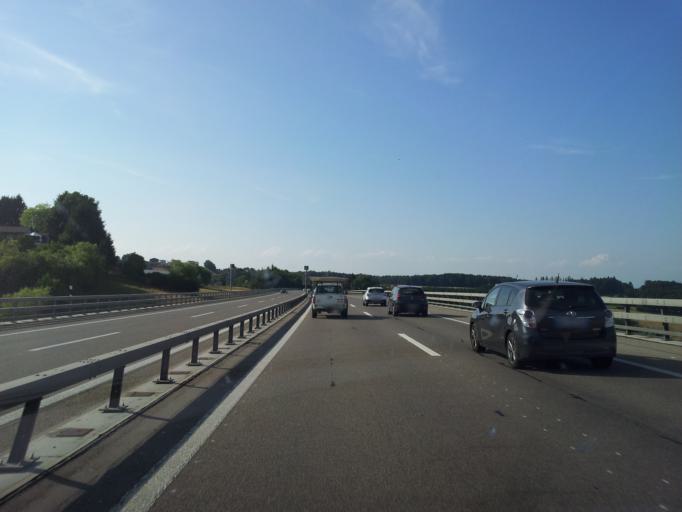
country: CH
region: Fribourg
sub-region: Gruyere District
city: La Roche
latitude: 46.6962
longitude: 7.0909
